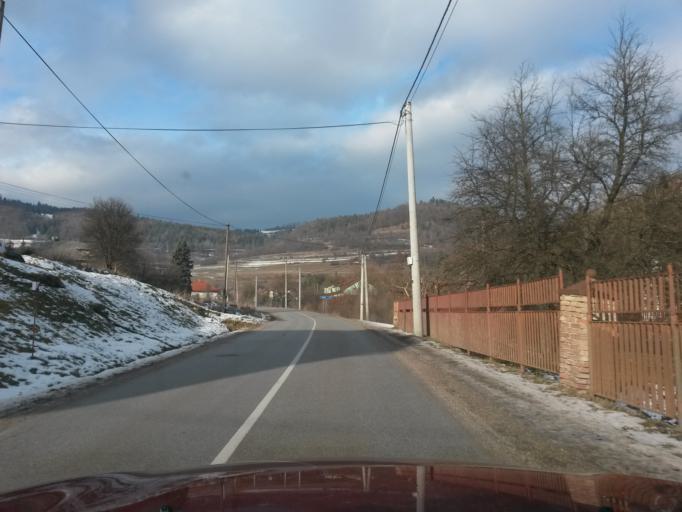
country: SK
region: Kosicky
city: Spisska Nova Ves
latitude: 48.8463
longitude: 20.6130
